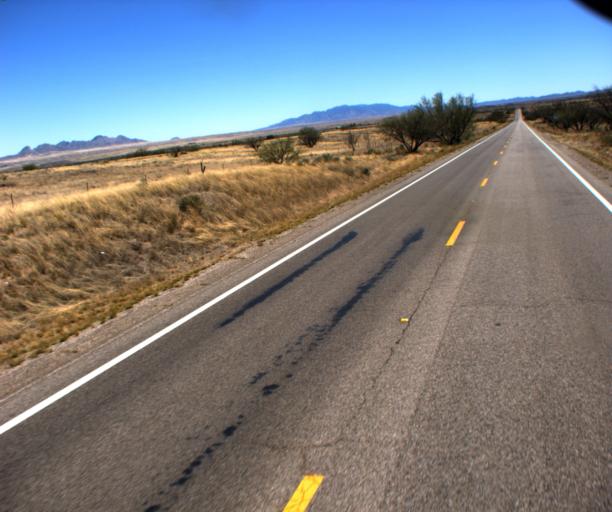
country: US
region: Arizona
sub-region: Pima County
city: Corona de Tucson
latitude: 31.7604
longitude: -110.6775
